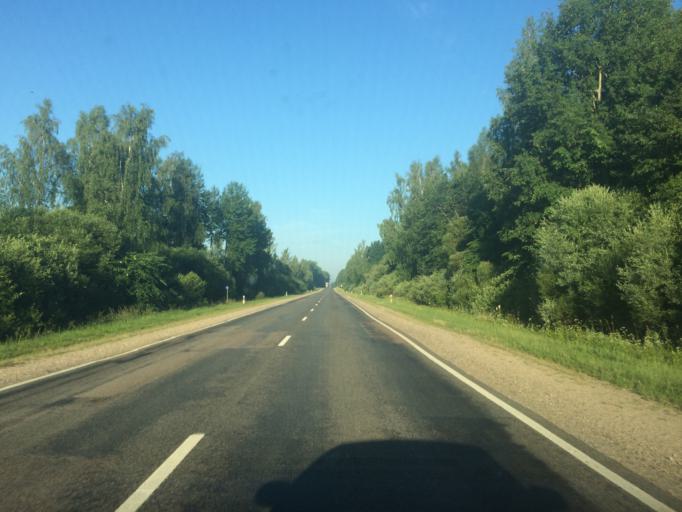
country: LT
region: Utenos apskritis
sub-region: Anyksciai
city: Anyksciai
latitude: 55.3610
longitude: 24.9844
